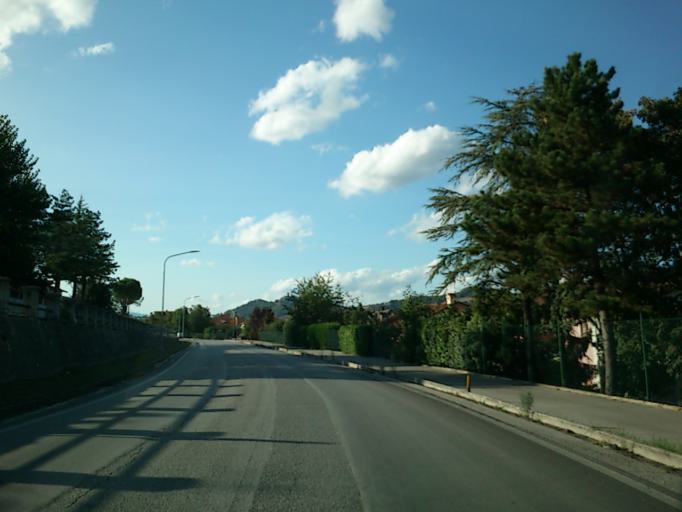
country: IT
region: The Marches
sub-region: Provincia di Pesaro e Urbino
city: Urbania
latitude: 43.6694
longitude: 12.5166
